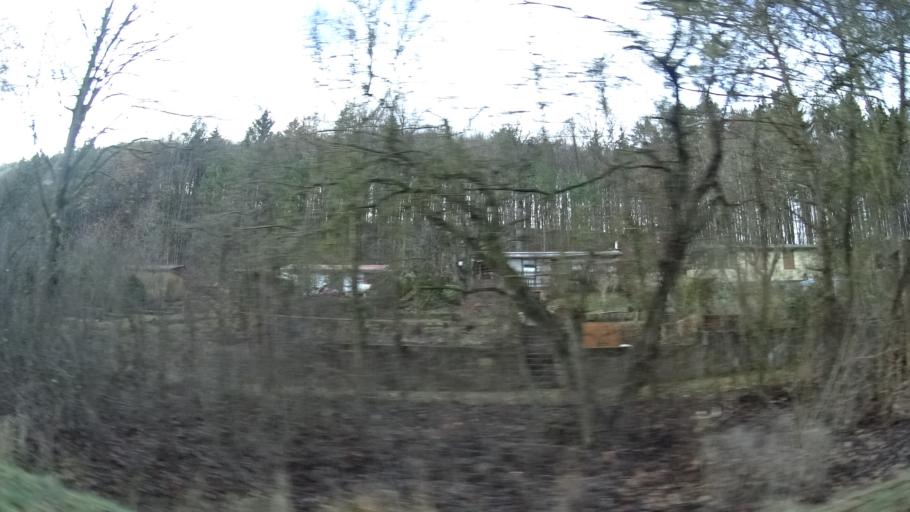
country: DE
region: Thuringia
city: Walldorf
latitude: 50.5936
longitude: 10.3977
